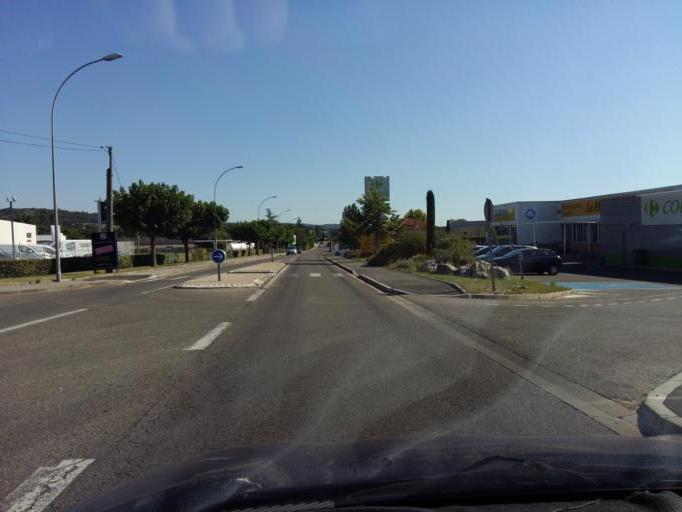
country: FR
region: Provence-Alpes-Cote d'Azur
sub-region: Departement du Vaucluse
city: Valreas
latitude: 44.3783
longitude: 4.9823
